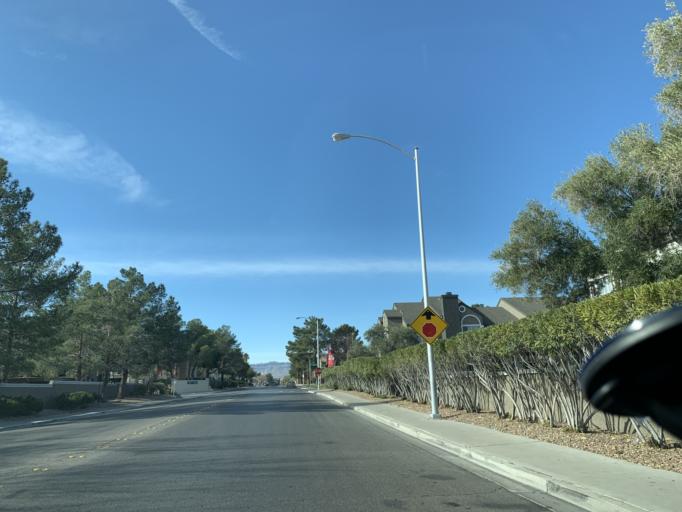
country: US
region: Nevada
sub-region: Clark County
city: Spring Valley
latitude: 36.0968
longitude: -115.2155
